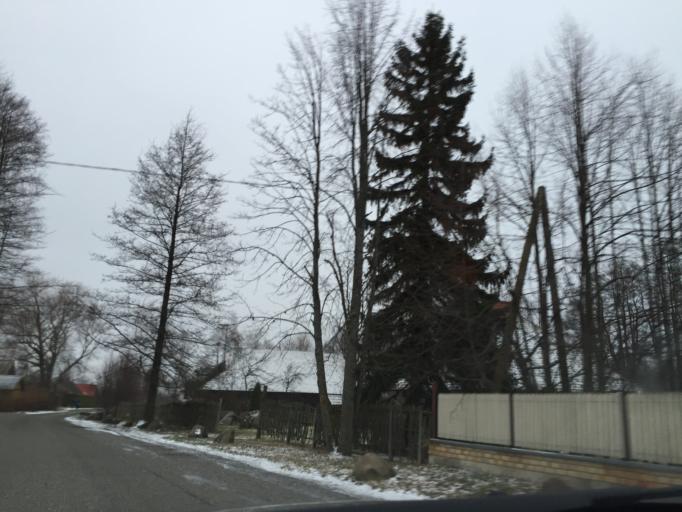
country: LV
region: Saulkrastu
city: Saulkrasti
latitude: 57.4938
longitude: 24.3870
